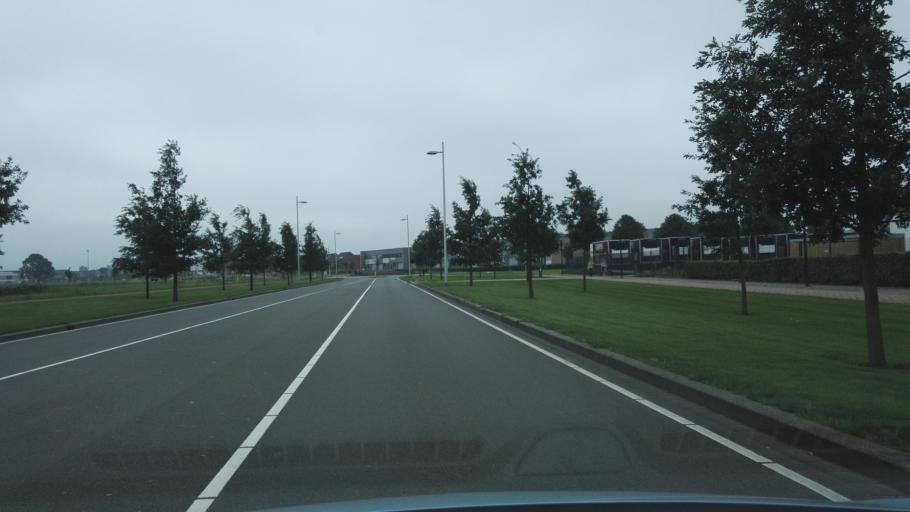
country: NL
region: Gelderland
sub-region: Gemeente Apeldoorn
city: Apeldoorn
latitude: 52.2449
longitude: 5.9901
